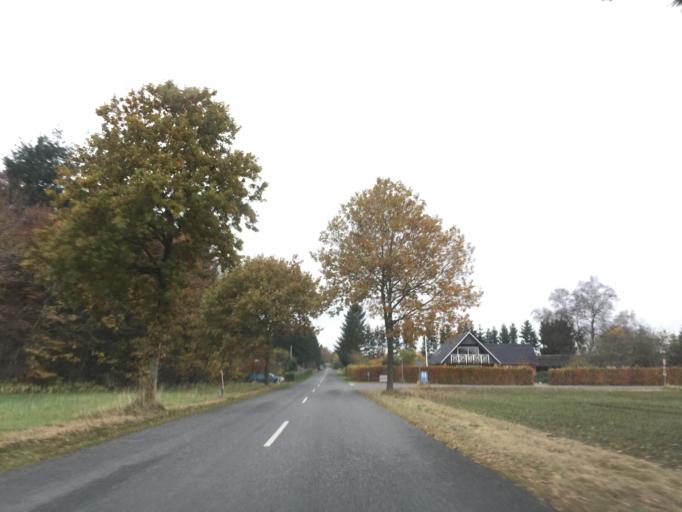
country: DK
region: Central Jutland
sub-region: Silkeborg Kommune
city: Svejbaek
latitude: 56.2387
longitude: 9.6634
